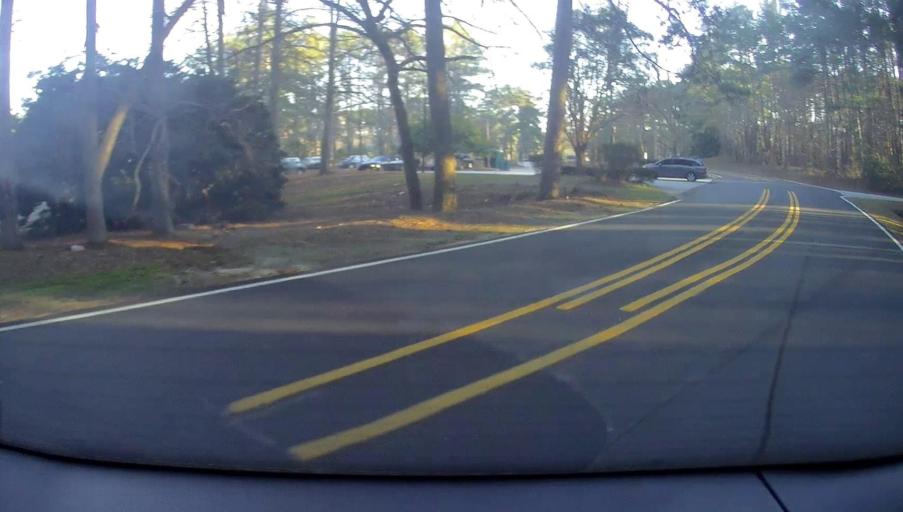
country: US
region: Georgia
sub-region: Fayette County
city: Peachtree City
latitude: 33.4018
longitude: -84.5872
